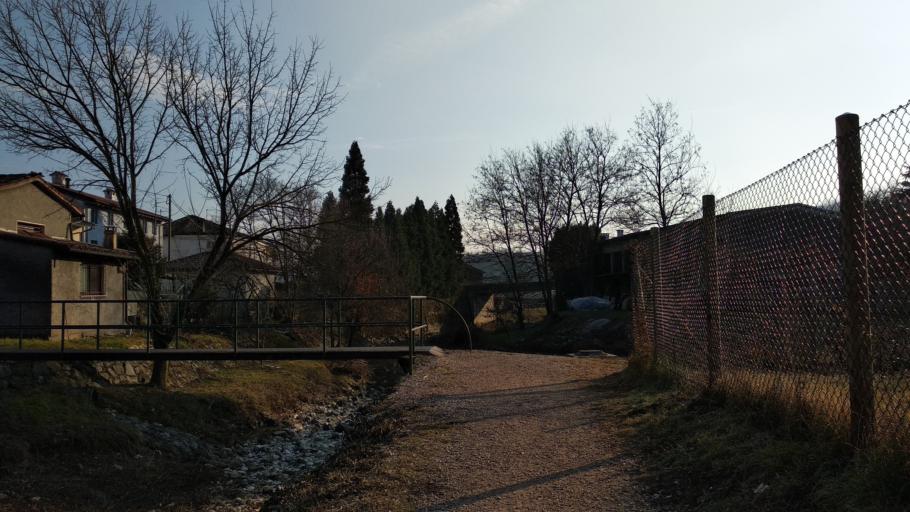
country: IT
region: Veneto
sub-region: Provincia di Vicenza
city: San Vito di Leguzzano
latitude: 45.6821
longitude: 11.3739
